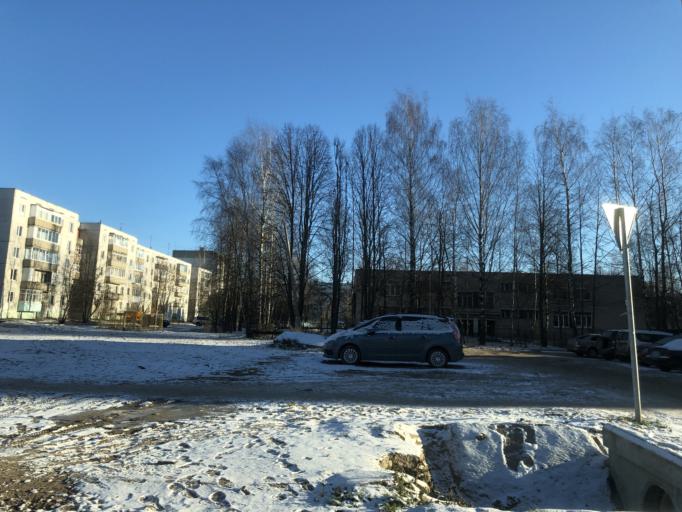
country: RU
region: Tverskaya
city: Rzhev
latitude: 56.2583
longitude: 34.3503
